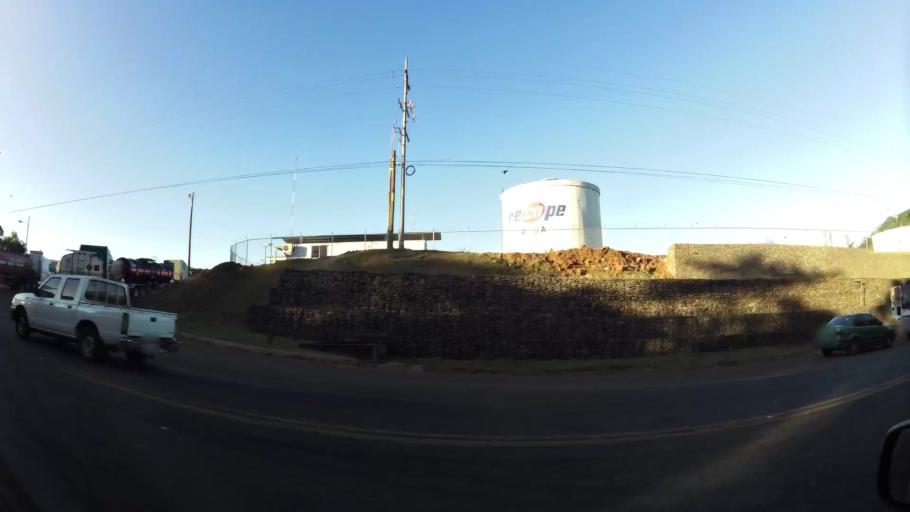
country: CR
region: Puntarenas
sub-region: Canton Central de Puntarenas
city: Chacarita
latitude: 10.0108
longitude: -84.7258
